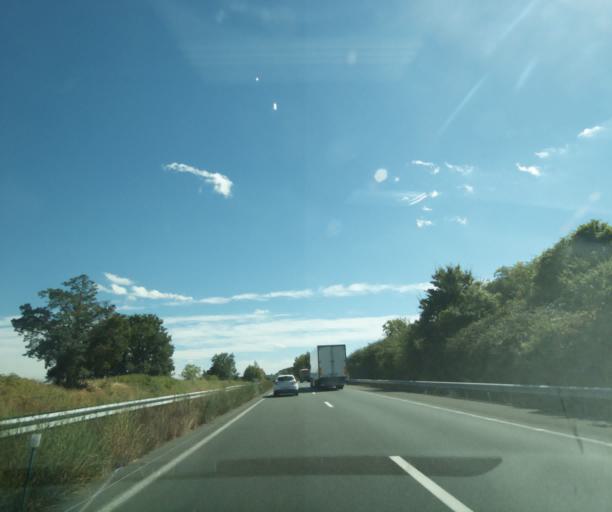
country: FR
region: Aquitaine
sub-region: Departement du Lot-et-Garonne
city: Buzet-sur-Baise
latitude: 44.2611
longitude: 0.2848
